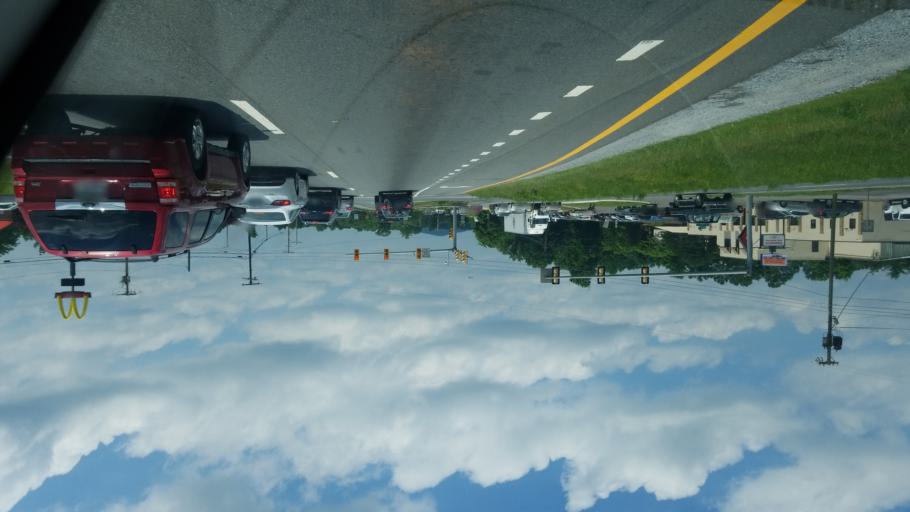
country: US
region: Virginia
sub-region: Campbell County
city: Rustburg
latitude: 37.2797
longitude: -79.1685
